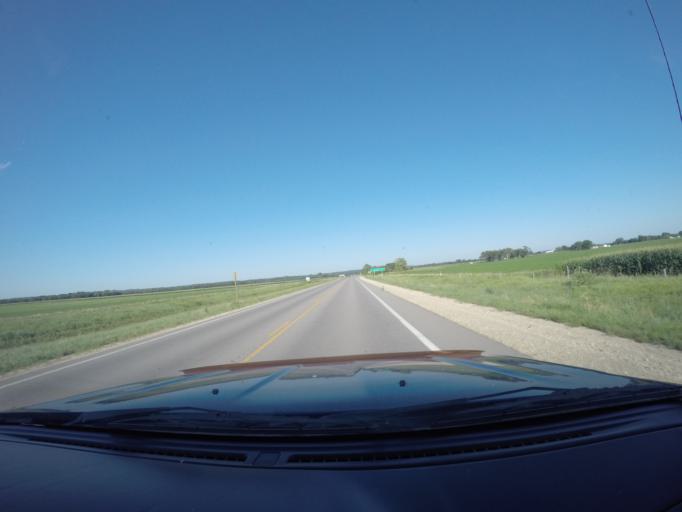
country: US
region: Kansas
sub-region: Jefferson County
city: Oskaloosa
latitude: 39.0873
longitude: -95.4315
